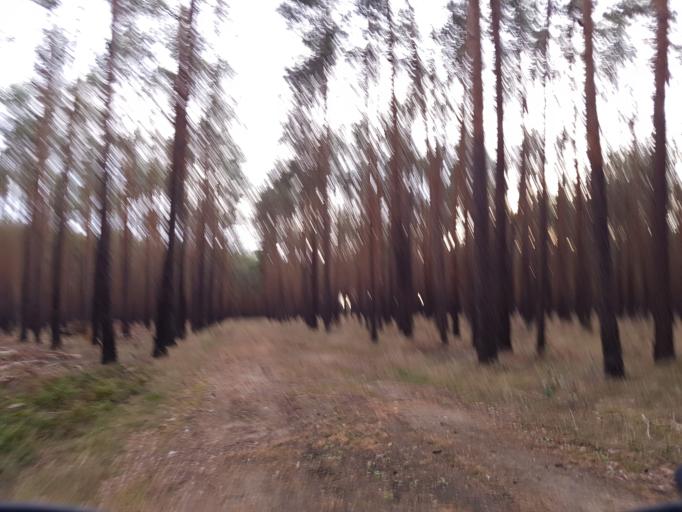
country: DE
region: Brandenburg
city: Trobitz
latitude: 51.5611
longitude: 13.4290
